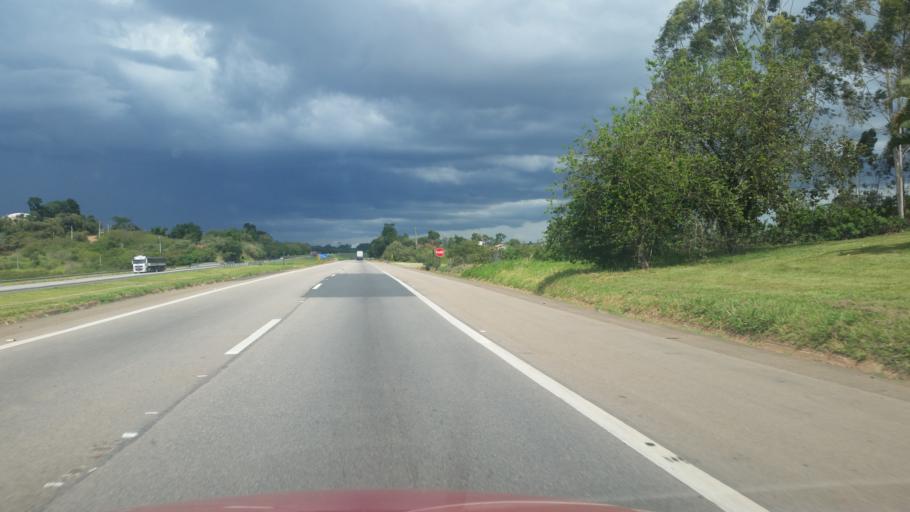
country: BR
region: Sao Paulo
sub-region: Boituva
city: Boituva
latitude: -23.2957
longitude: -47.7067
